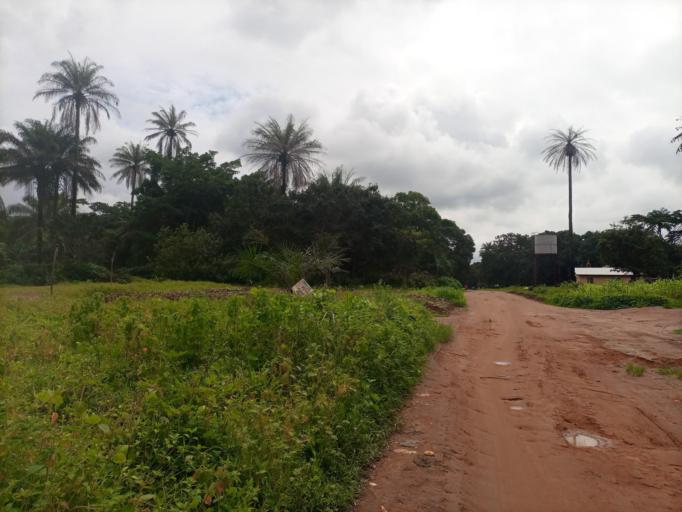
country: SL
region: Northern Province
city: Sawkta
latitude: 8.6364
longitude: -13.1937
